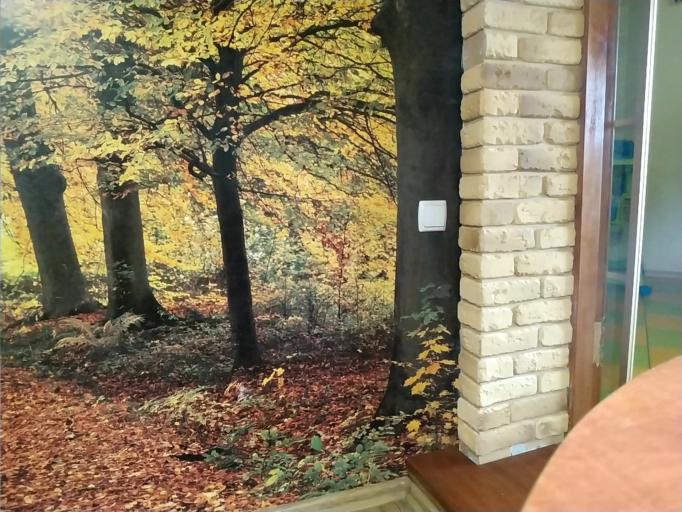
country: RU
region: Smolensk
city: Dorogobuzh
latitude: 54.8514
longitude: 33.3210
